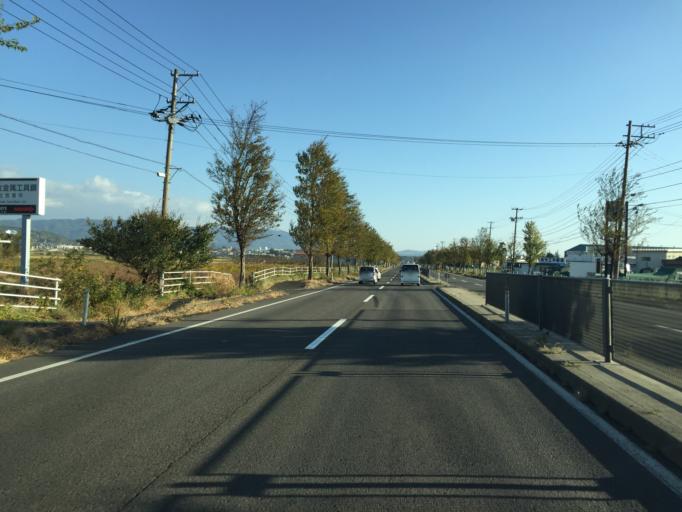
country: JP
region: Fukushima
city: Hobaramachi
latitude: 37.8264
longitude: 140.5103
